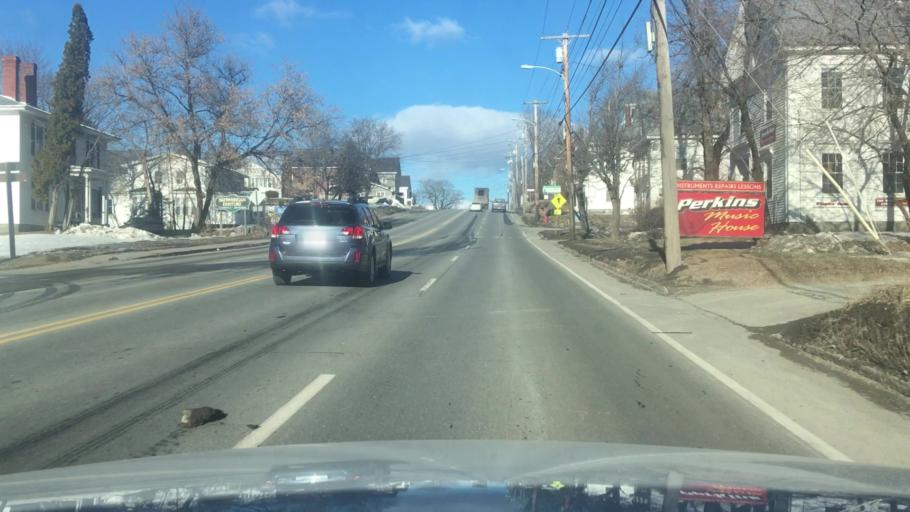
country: US
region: Maine
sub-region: Somerset County
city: Skowhegan
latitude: 44.7705
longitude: -69.7218
